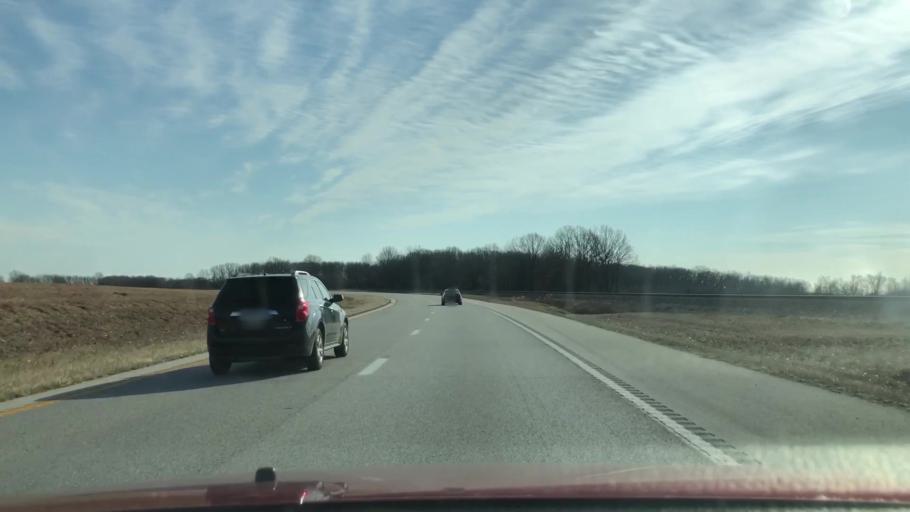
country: US
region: Missouri
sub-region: Webster County
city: Seymour
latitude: 37.1311
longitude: -92.7397
